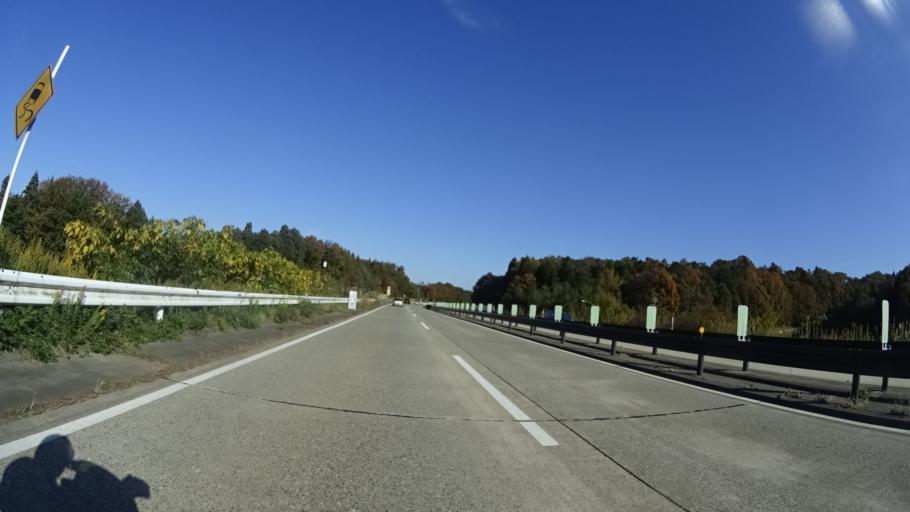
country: JP
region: Ishikawa
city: Komatsu
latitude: 36.3549
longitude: 136.4519
